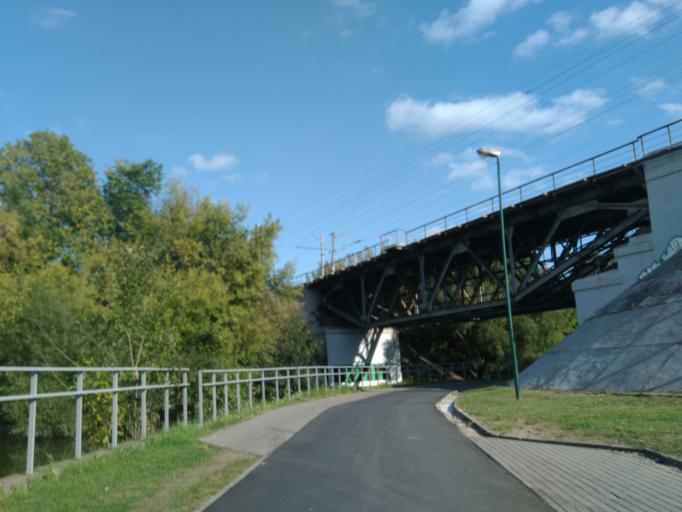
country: BY
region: Minsk
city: Minsk
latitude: 53.8884
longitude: 27.5713
